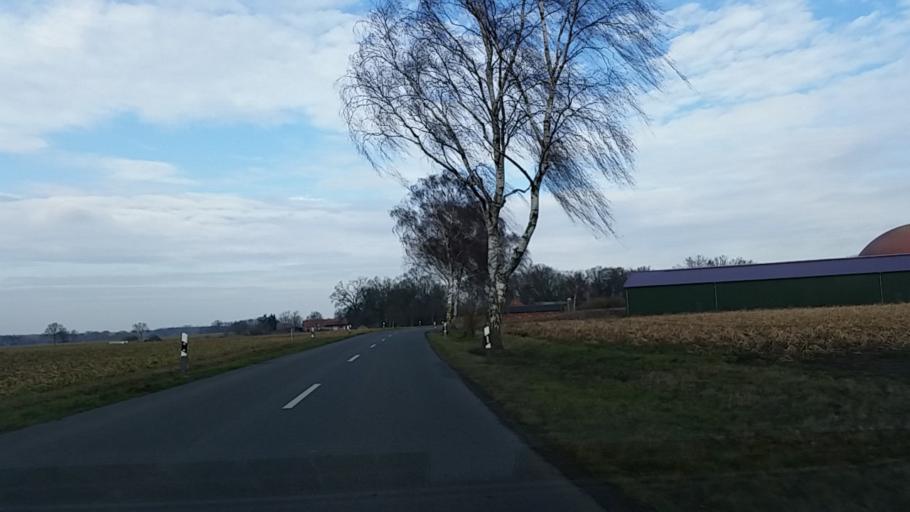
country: DE
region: Lower Saxony
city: Altenmedingen
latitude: 53.1320
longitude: 10.6364
